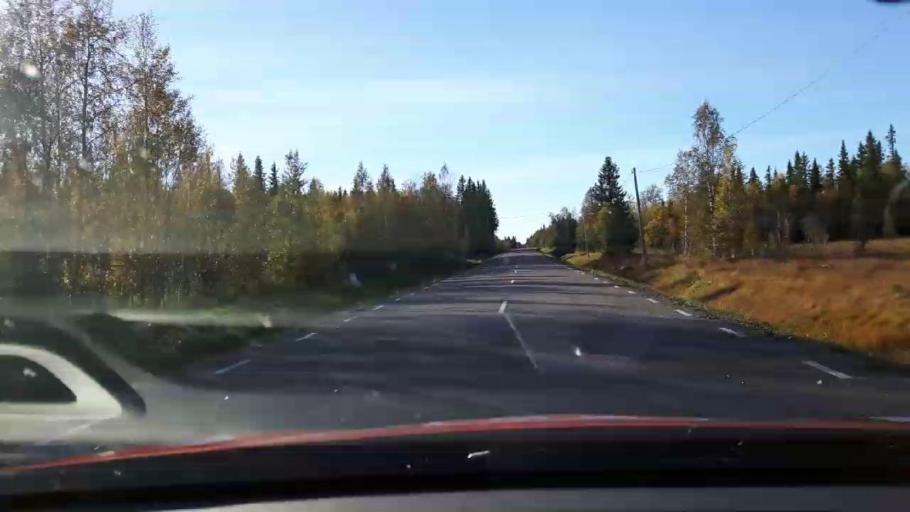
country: SE
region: Jaemtland
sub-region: Stroemsunds Kommun
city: Stroemsund
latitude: 63.8602
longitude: 15.1829
